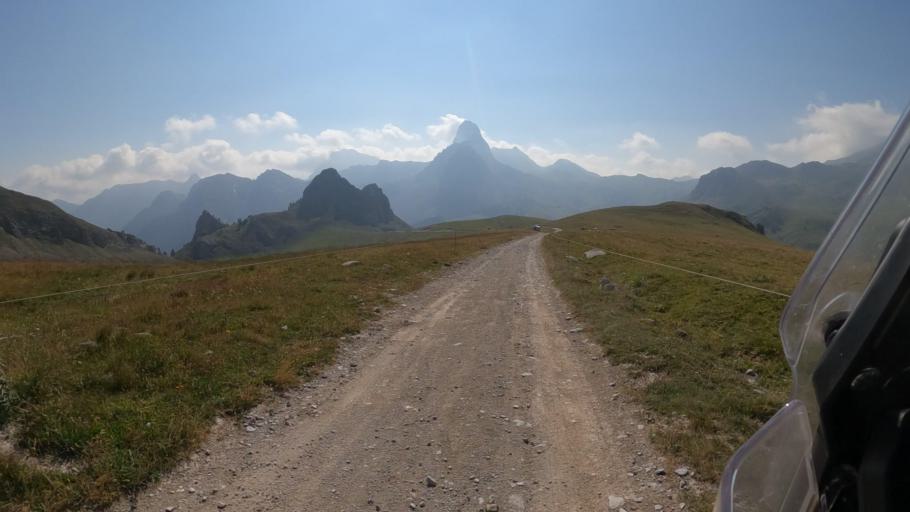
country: IT
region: Piedmont
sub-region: Provincia di Cuneo
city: Bersezio
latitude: 44.4059
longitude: 7.0242
